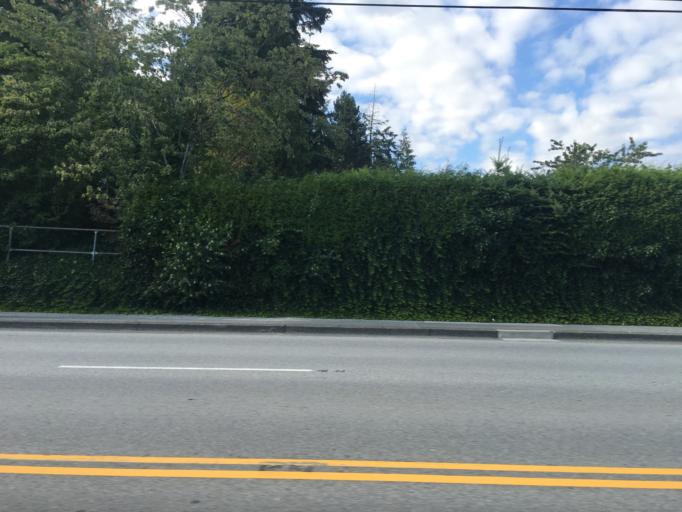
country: CA
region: British Columbia
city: Port Moody
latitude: 49.2490
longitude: -122.8495
